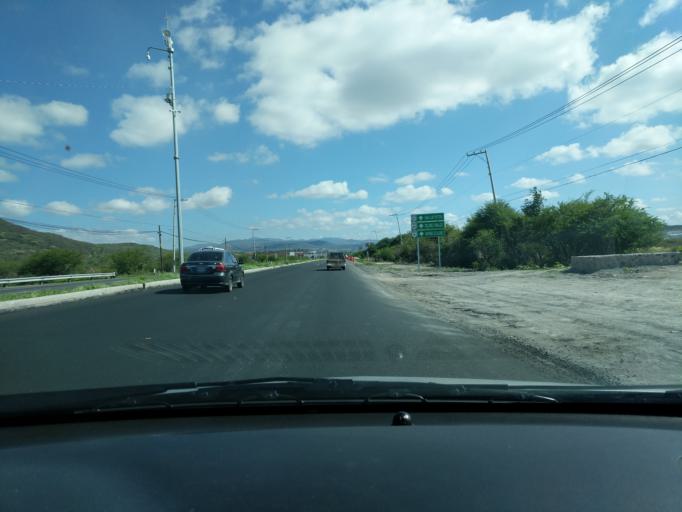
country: MX
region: Queretaro
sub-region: Queretaro
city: Patria Nueva
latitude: 20.6316
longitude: -100.4991
